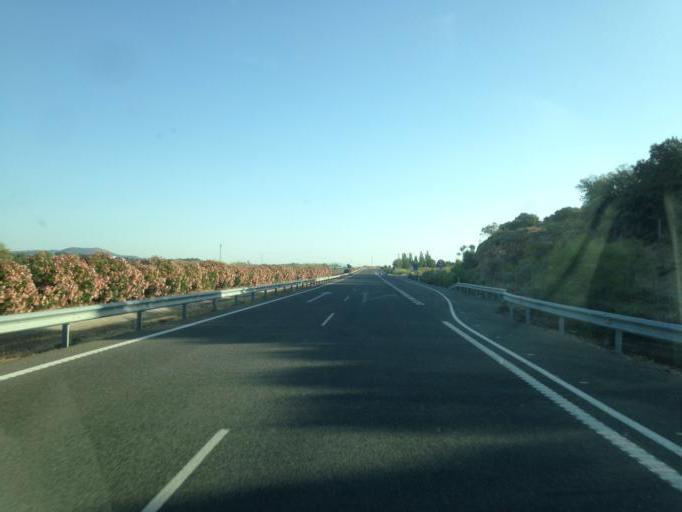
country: ES
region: Andalusia
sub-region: Provincia de Malaga
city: Villanueva del Trabuco
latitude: 37.0911
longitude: -4.3156
